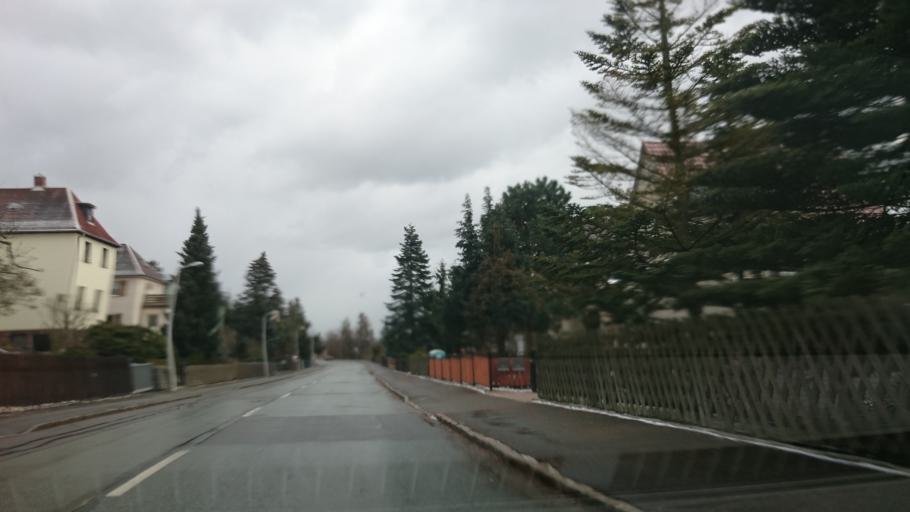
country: DE
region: Saxony
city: Hartmannsdorf
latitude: 50.7319
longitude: 12.4393
